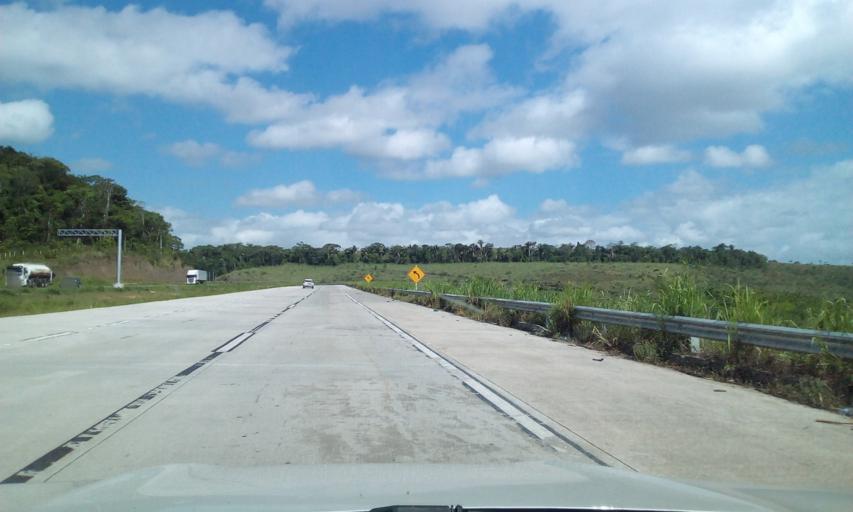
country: BR
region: Alagoas
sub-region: Rio Largo
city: Rio Largo
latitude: -9.5033
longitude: -35.9122
